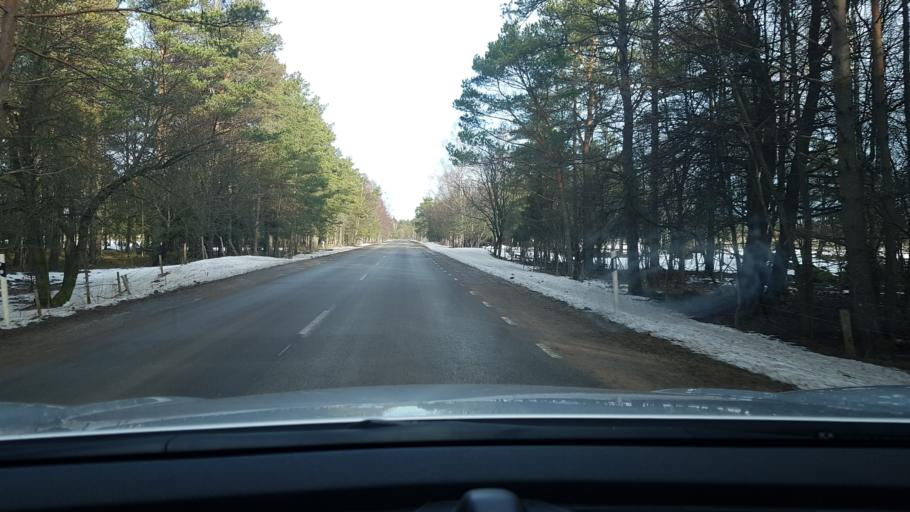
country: EE
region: Saare
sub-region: Kuressaare linn
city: Kuressaare
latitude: 58.4746
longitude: 22.7031
